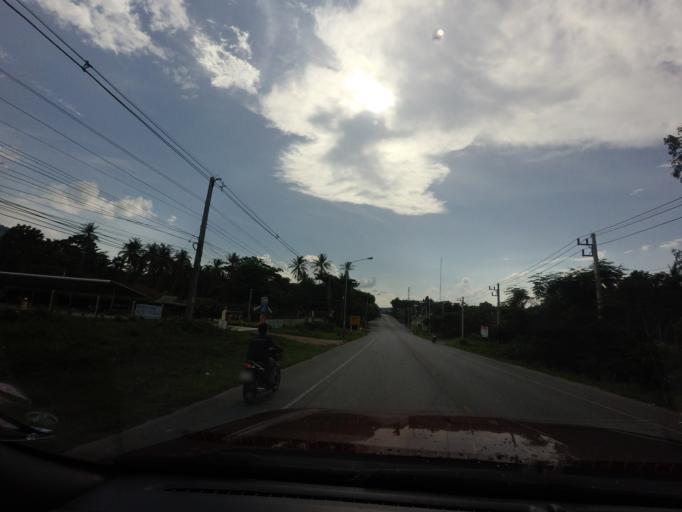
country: TH
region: Pattani
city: Khok Pho
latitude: 6.6737
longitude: 101.1542
